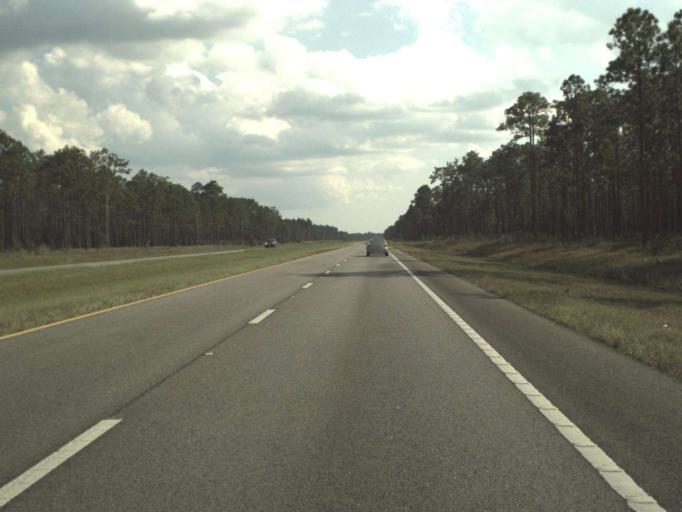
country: US
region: Florida
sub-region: Bay County
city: Laguna Beach
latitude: 30.3857
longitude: -85.8705
